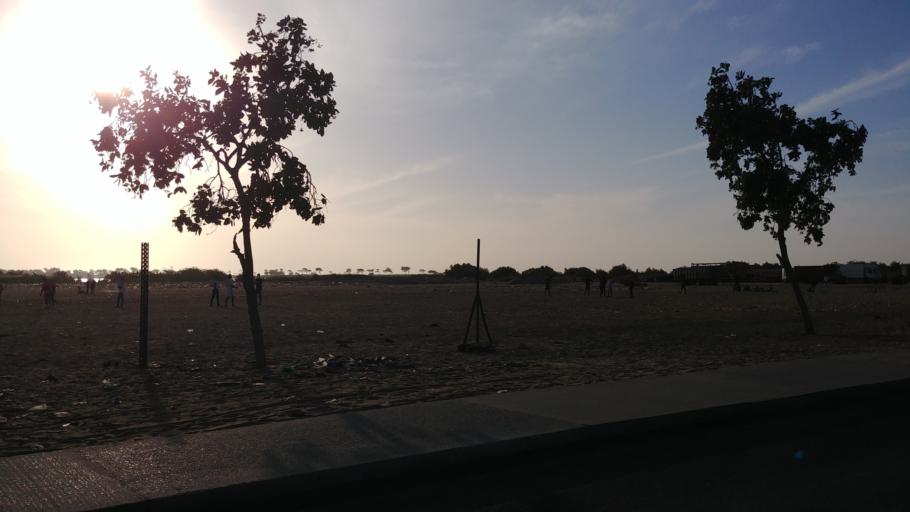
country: SN
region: Saint-Louis
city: Saint-Louis
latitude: 16.0126
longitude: -16.4968
